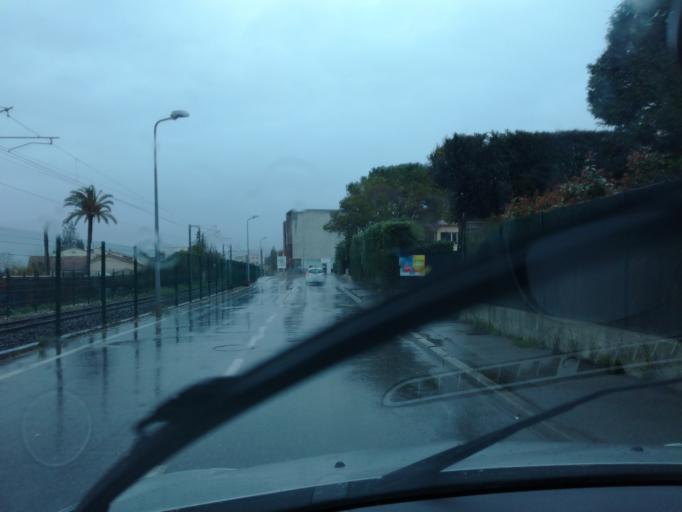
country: FR
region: Provence-Alpes-Cote d'Azur
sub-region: Departement des Alpes-Maritimes
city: Mouans-Sartoux
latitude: 43.6167
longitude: 6.9755
